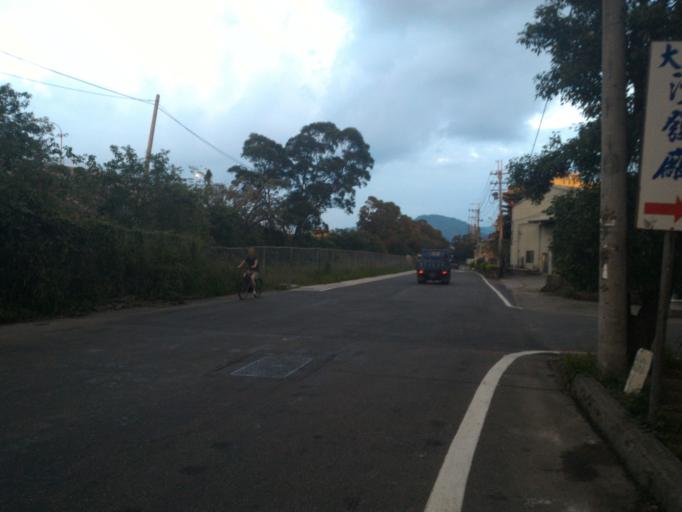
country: TW
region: Taiwan
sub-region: Taoyuan
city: Taoyuan
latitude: 24.9511
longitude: 121.3901
